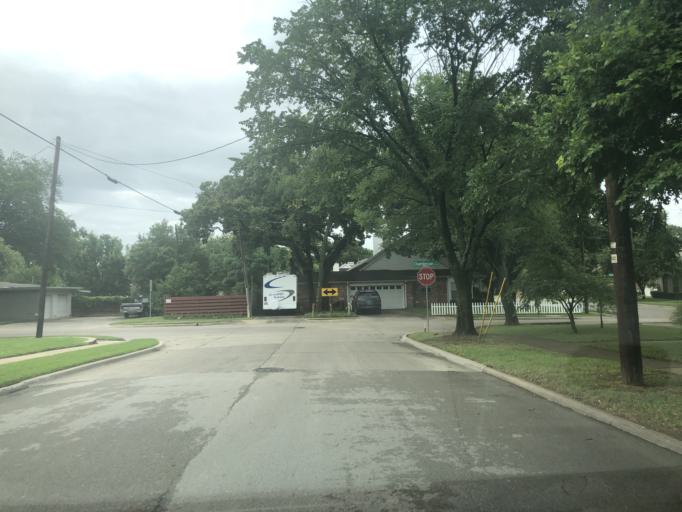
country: US
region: Texas
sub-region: Dallas County
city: Irving
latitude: 32.8034
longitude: -96.9425
